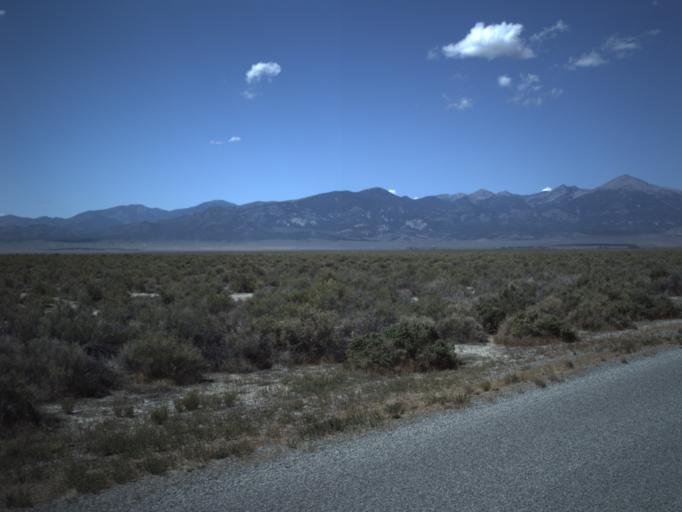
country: US
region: Nevada
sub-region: White Pine County
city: McGill
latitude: 39.0523
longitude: -113.9853
